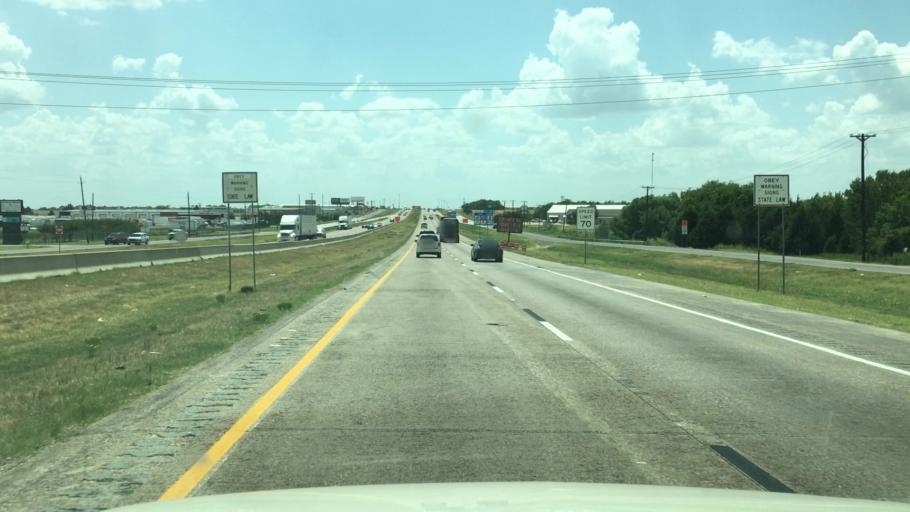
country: US
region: Texas
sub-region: Rockwall County
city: Fate
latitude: 32.9284
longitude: -96.3897
